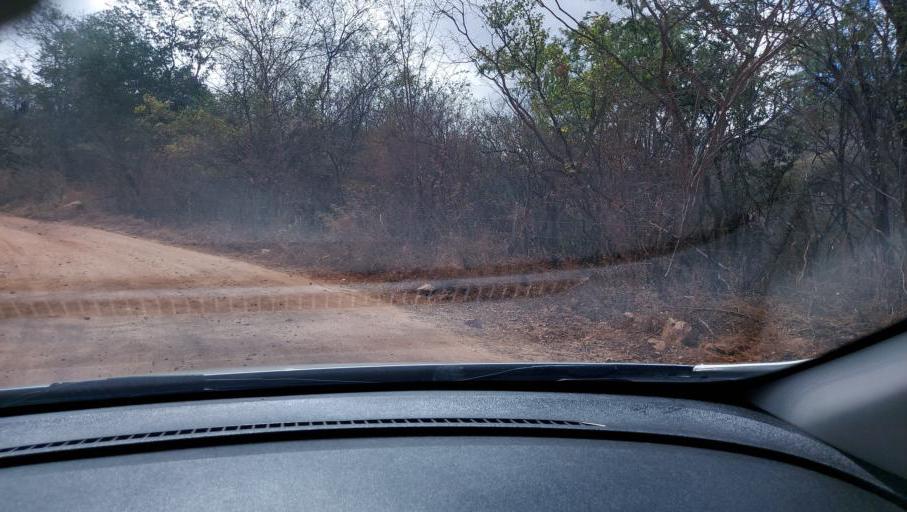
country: BR
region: Bahia
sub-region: Oliveira Dos Brejinhos
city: Beira Rio
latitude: -12.0973
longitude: -42.5476
